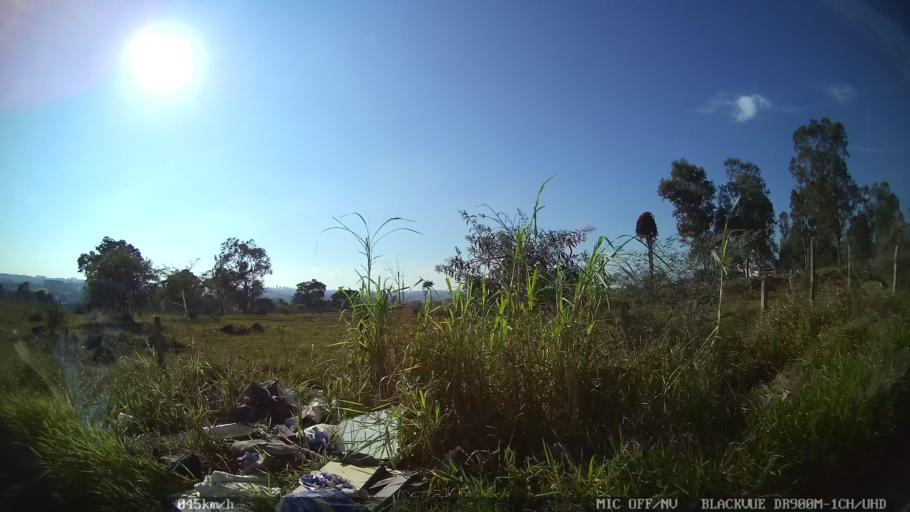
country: BR
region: Sao Paulo
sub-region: Campinas
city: Campinas
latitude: -22.9712
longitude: -47.1104
